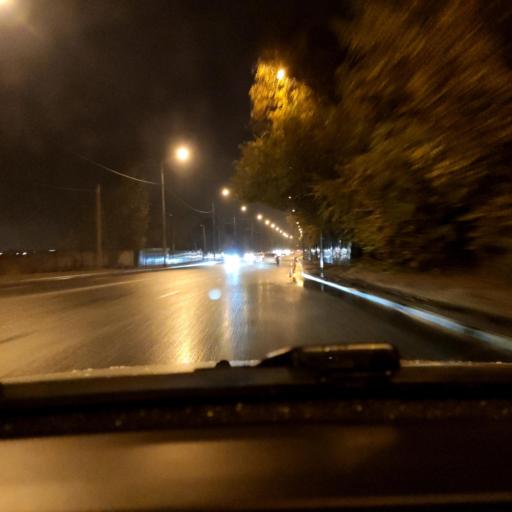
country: RU
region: Voronezj
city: Voronezh
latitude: 51.6916
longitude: 39.2327
